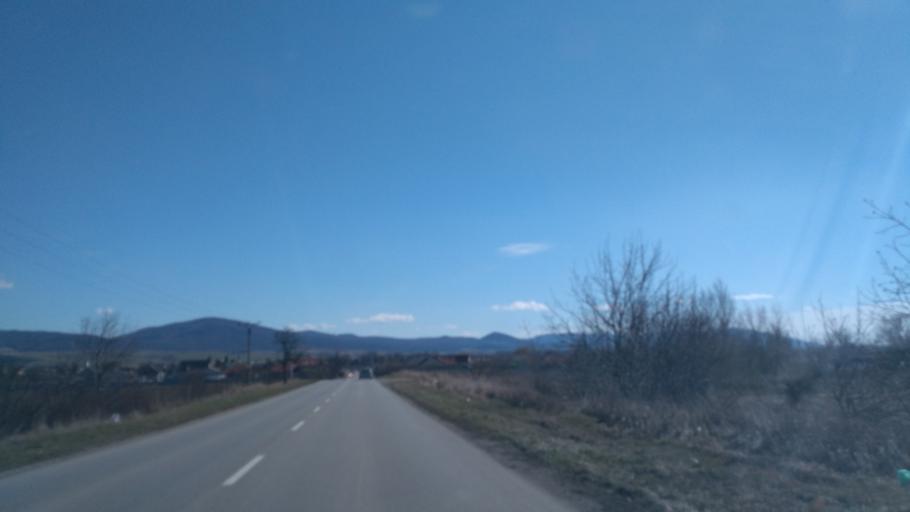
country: SK
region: Kosicky
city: Kosice
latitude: 48.6178
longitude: 21.3142
